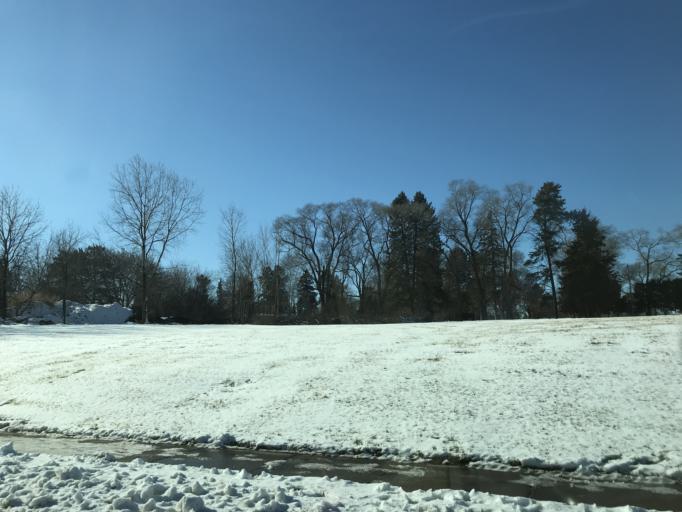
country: US
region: Wisconsin
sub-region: Dane County
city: Monona
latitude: 43.0507
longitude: -89.3169
